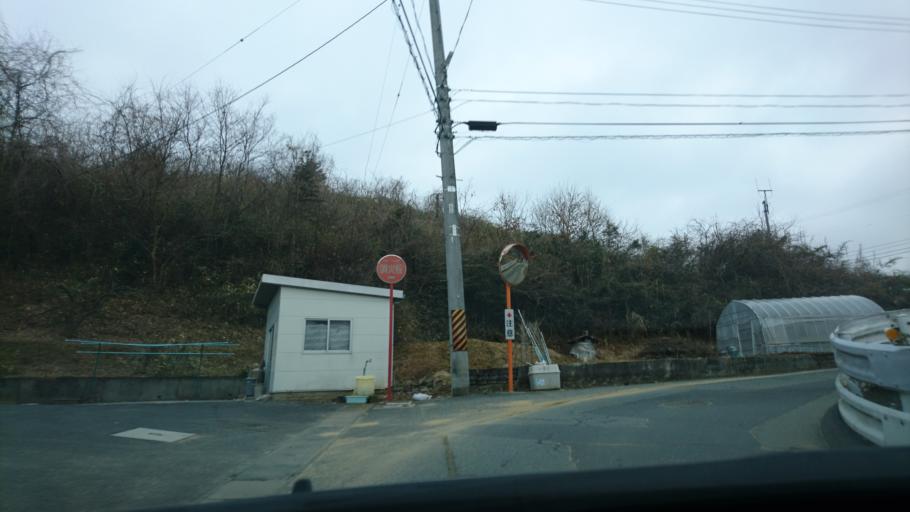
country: JP
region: Iwate
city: Ichinoseki
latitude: 38.9236
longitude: 141.3380
